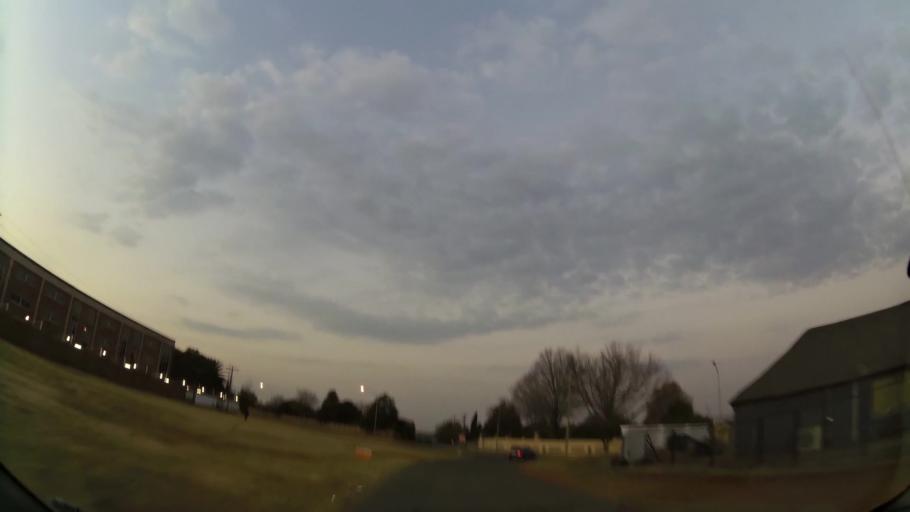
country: ZA
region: Gauteng
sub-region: Ekurhuleni Metropolitan Municipality
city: Benoni
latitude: -26.1396
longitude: 28.3134
